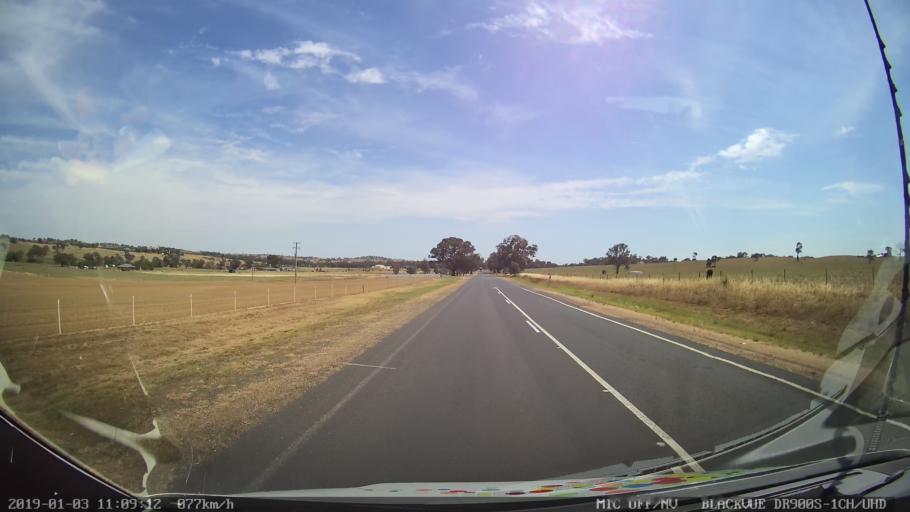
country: AU
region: New South Wales
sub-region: Young
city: Young
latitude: -34.2411
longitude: 148.2553
